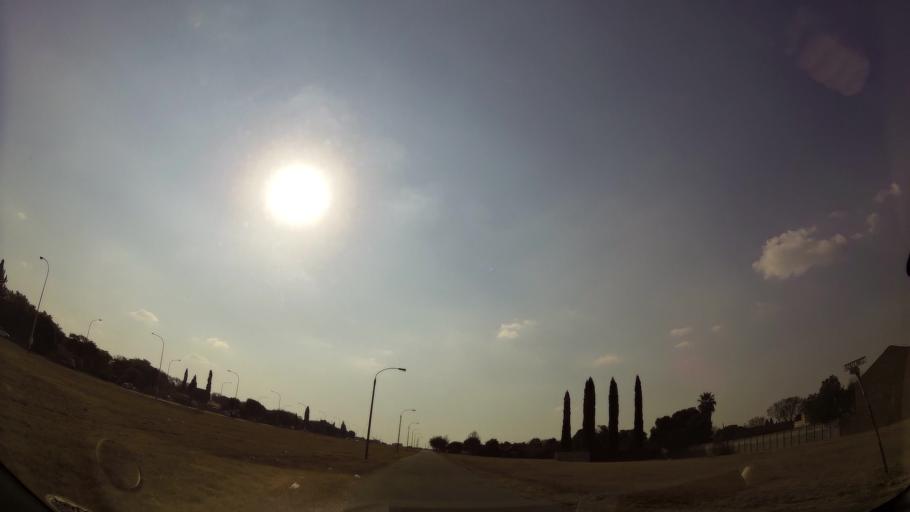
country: ZA
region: Gauteng
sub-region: Ekurhuleni Metropolitan Municipality
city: Benoni
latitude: -26.1647
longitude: 28.2792
